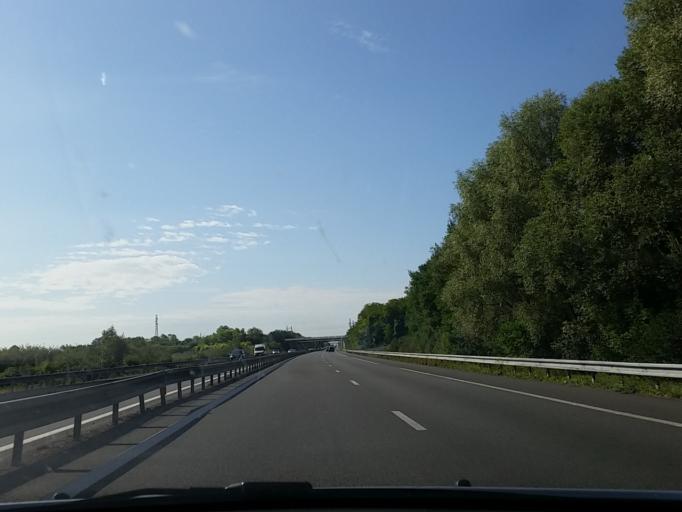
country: FR
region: Centre
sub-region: Departement du Cher
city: Foecy
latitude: 47.1671
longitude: 2.1815
